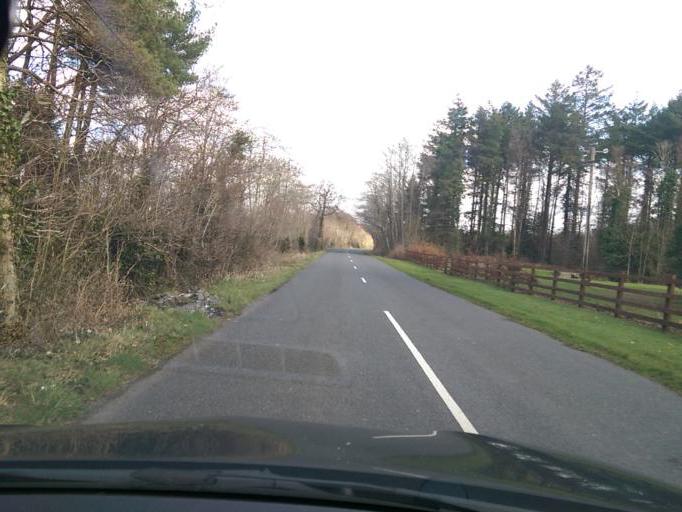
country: IE
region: Connaught
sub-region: County Galway
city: Athenry
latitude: 53.4666
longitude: -8.5313
